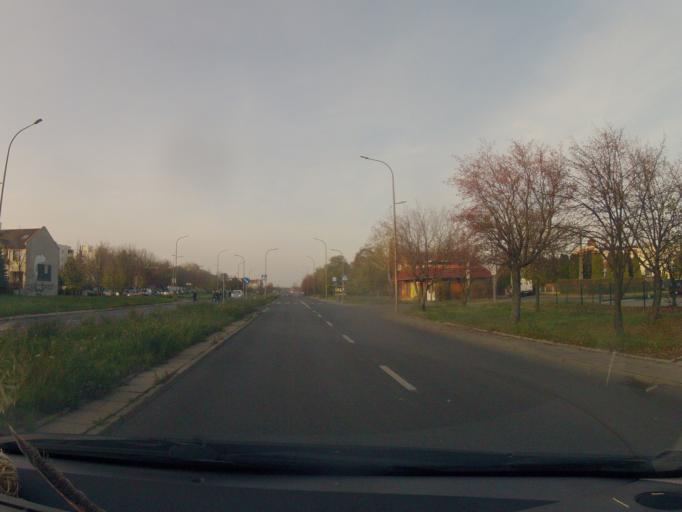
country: PL
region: Opole Voivodeship
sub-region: Powiat opolski
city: Opole
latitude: 50.6718
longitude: 17.9755
